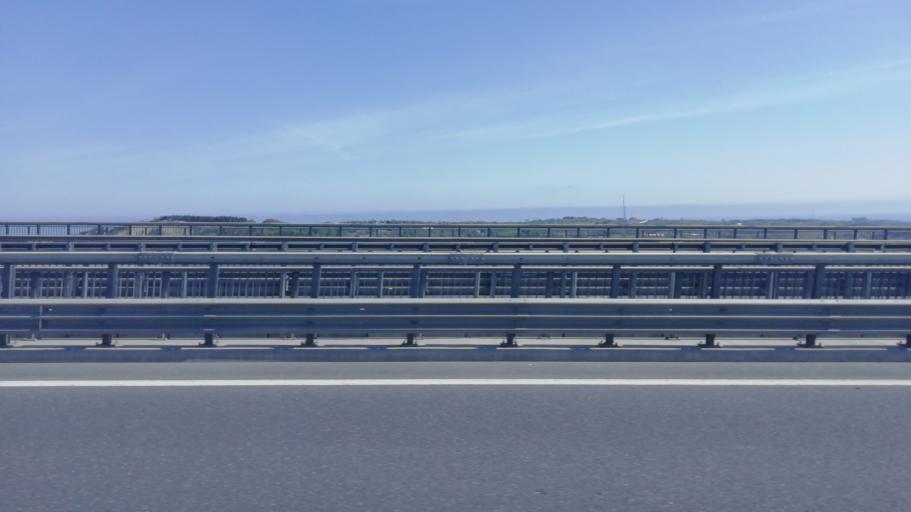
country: TR
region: Istanbul
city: Arikoey
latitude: 41.2320
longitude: 28.9667
